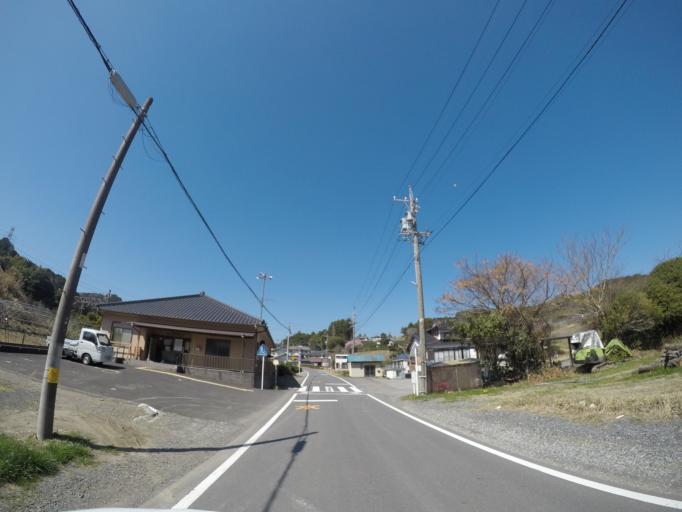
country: JP
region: Shizuoka
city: Kanaya
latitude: 34.7929
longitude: 138.1271
